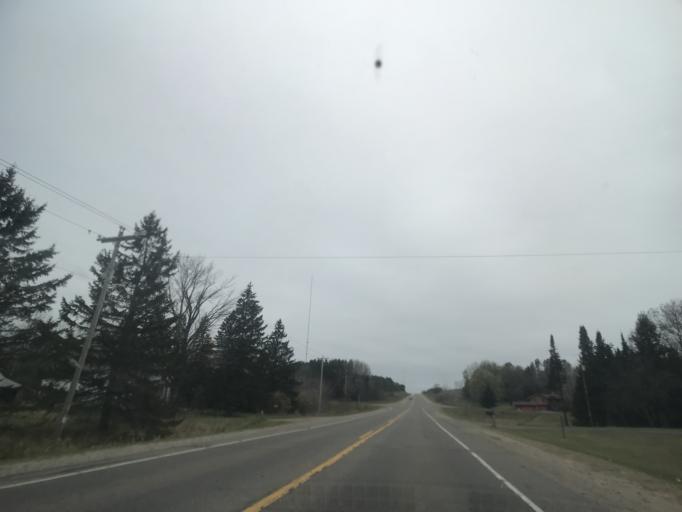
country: US
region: Wisconsin
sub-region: Oconto County
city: Gillett
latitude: 44.9991
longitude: -88.3855
